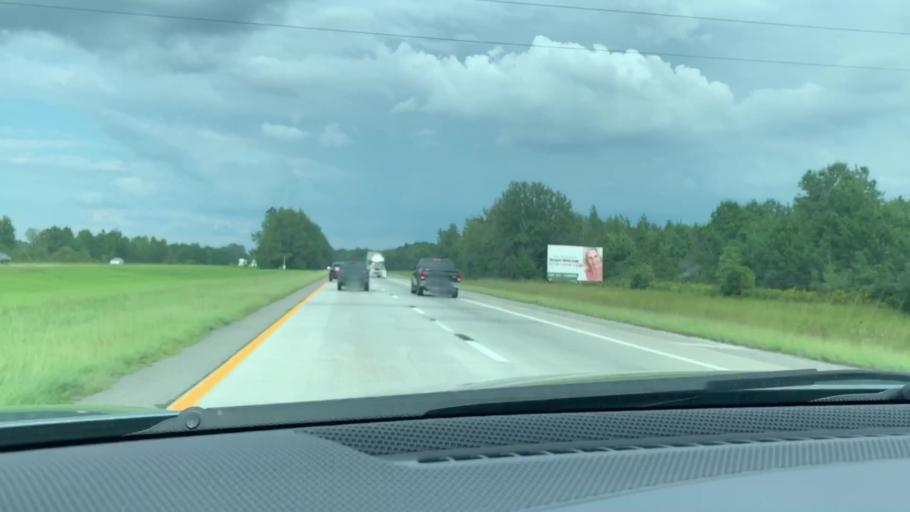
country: US
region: South Carolina
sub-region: Dorchester County
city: Saint George
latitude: 33.1364
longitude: -80.6328
